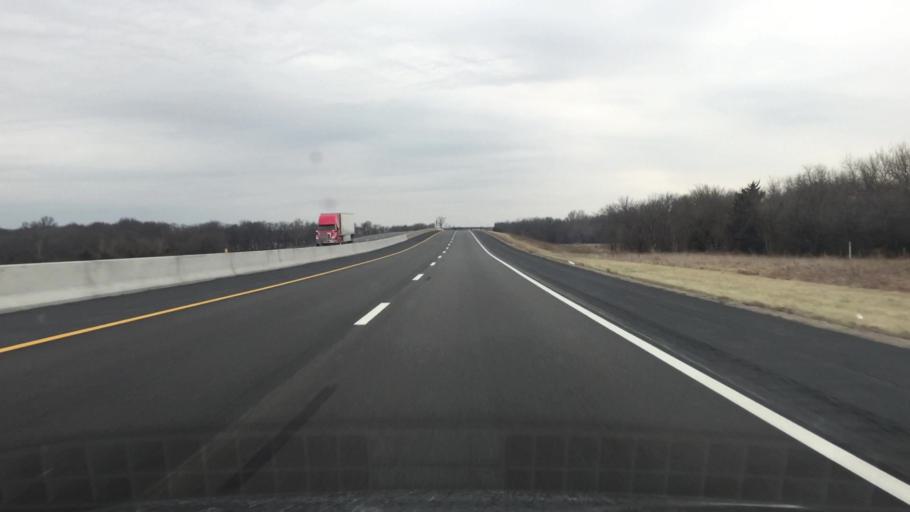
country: US
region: Kansas
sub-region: Shawnee County
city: Auburn
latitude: 38.7763
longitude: -95.9212
